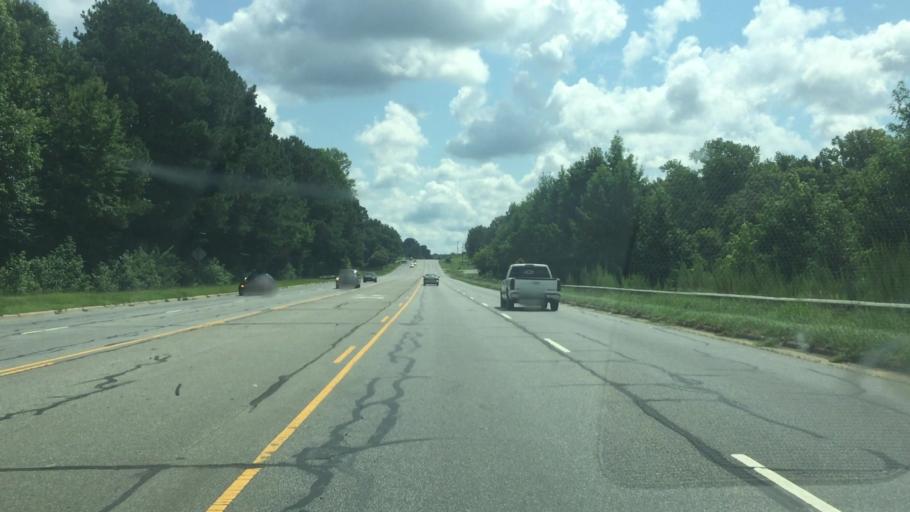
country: US
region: North Carolina
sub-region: Anson County
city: Wadesboro
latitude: 34.9632
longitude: -80.0369
